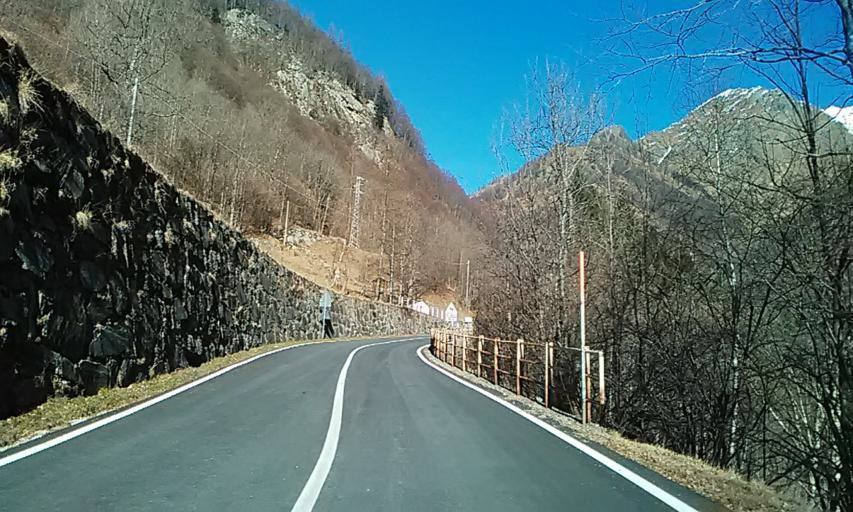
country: IT
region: Piedmont
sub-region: Provincia di Vercelli
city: Rimasco
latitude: 45.8847
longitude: 8.0664
